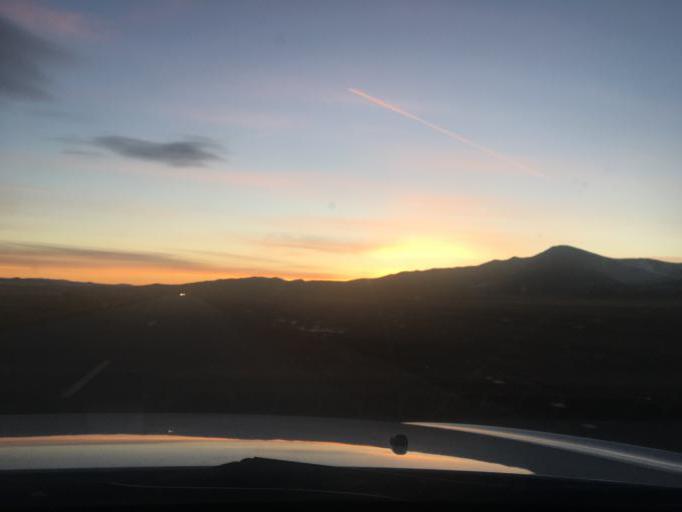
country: MN
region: Central Aimak
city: Mandal
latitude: 48.0915
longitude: 106.6039
